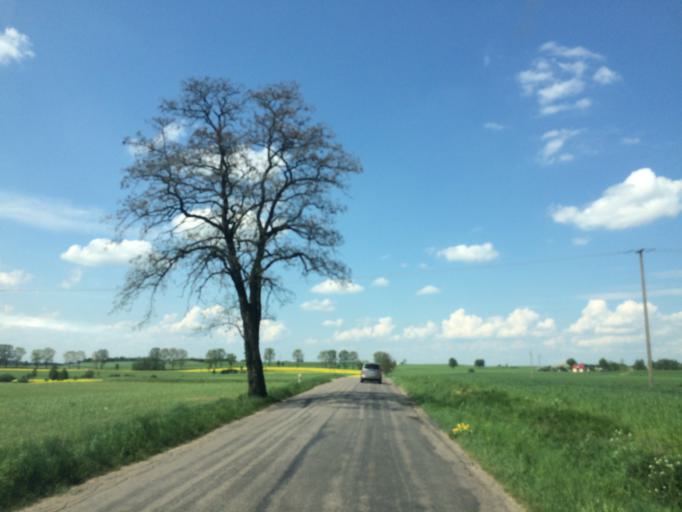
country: PL
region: Warmian-Masurian Voivodeship
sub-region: Powiat dzialdowski
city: Rybno
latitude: 53.3959
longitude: 19.8887
